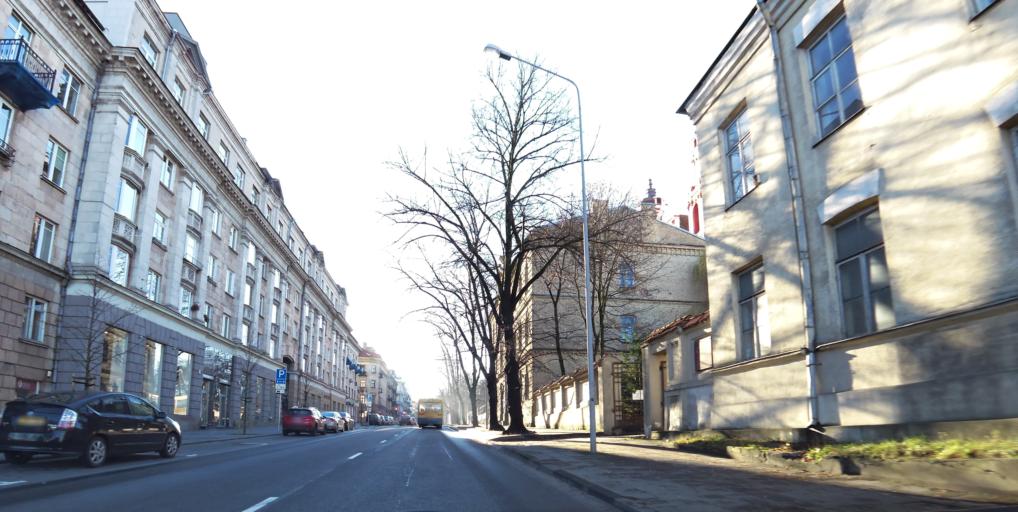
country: LT
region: Vilnius County
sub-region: Vilnius
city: Vilnius
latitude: 54.6913
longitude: 25.2732
